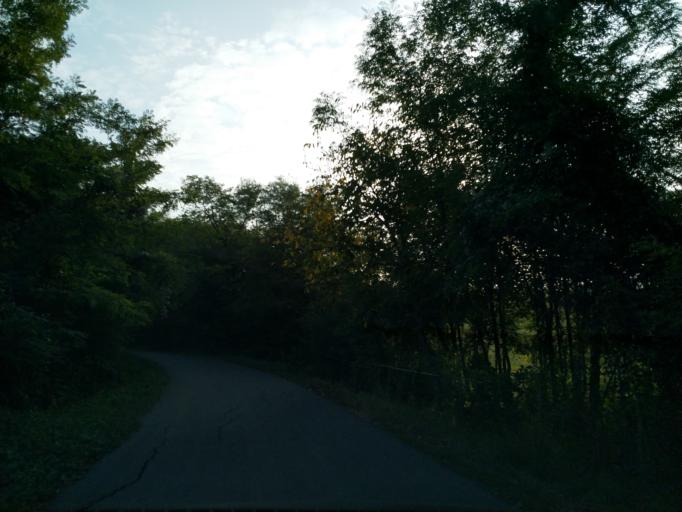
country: RS
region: Central Serbia
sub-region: Sumadijski Okrug
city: Arangelovac
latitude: 44.3116
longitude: 20.5912
